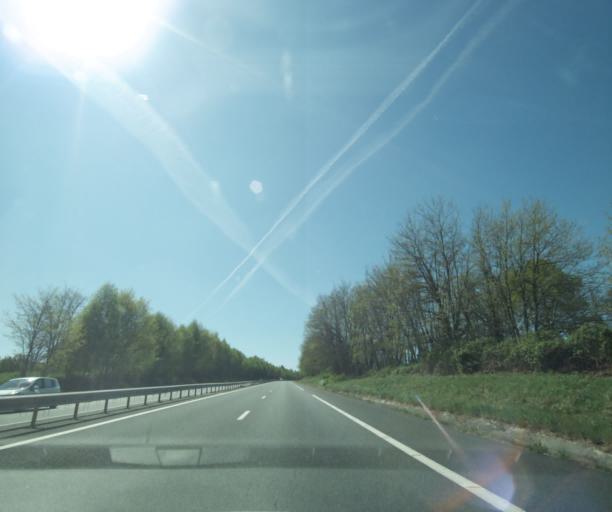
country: FR
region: Limousin
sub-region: Departement de la Haute-Vienne
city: Saint-Sulpice-les-Feuilles
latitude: 46.3761
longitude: 1.4456
